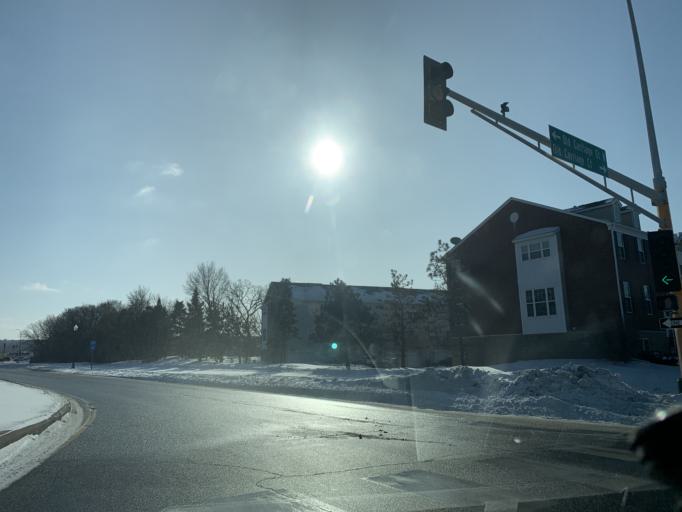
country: US
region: Minnesota
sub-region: Scott County
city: Prior Lake
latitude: 44.7756
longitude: -93.4174
